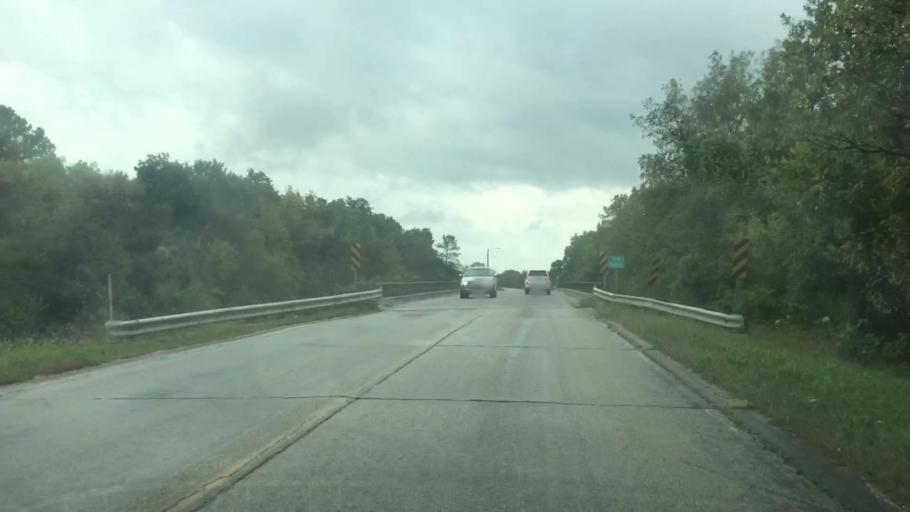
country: US
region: Kansas
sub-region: Allen County
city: Iola
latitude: 37.9098
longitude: -95.4094
